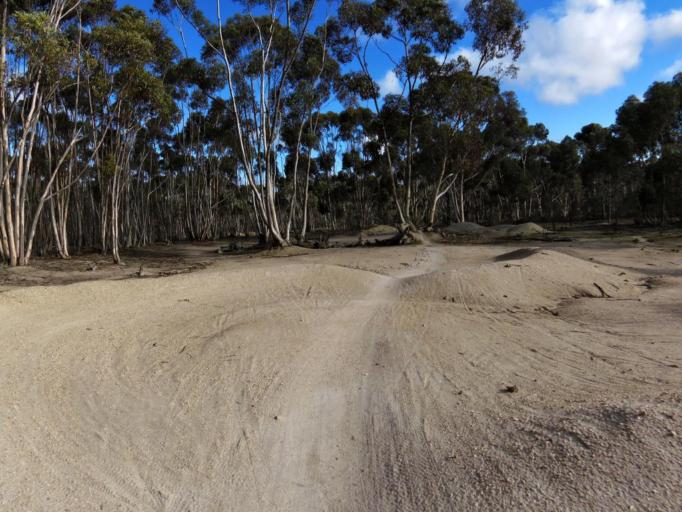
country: AU
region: Victoria
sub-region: Greater Geelong
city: Lara
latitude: -37.9396
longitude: 144.4085
